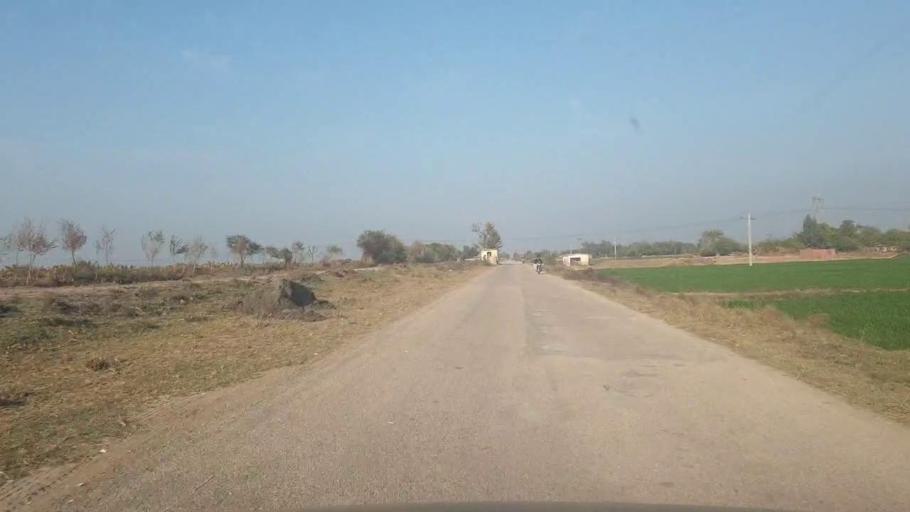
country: PK
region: Sindh
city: Sakrand
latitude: 26.0589
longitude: 68.3451
